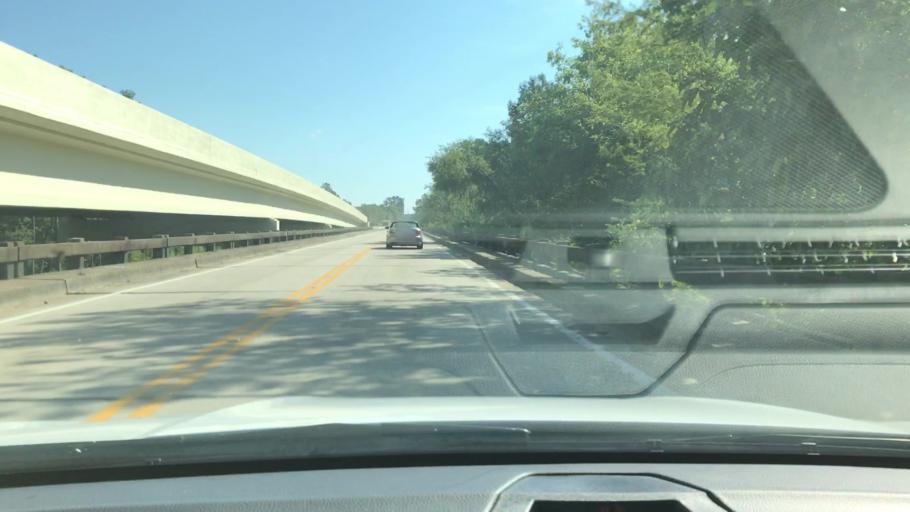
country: US
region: South Carolina
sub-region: Horry County
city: Socastee
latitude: 33.6679
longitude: -79.1438
